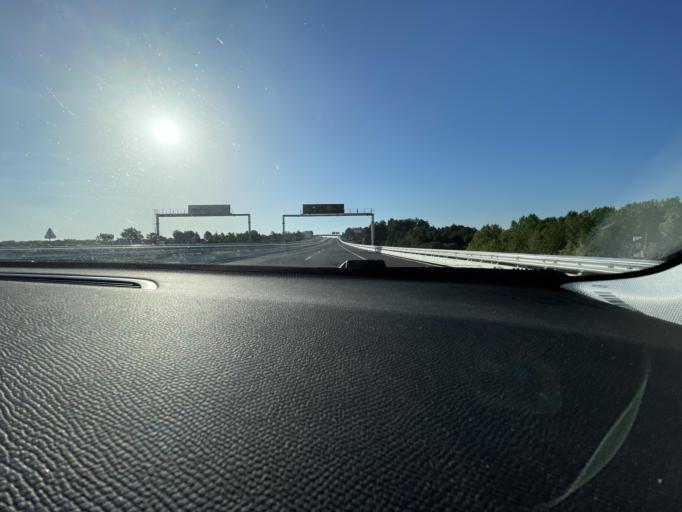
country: ES
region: Castille and Leon
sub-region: Provincia de Salamanca
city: Fuentes de Onoro
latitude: 40.6167
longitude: -6.8300
